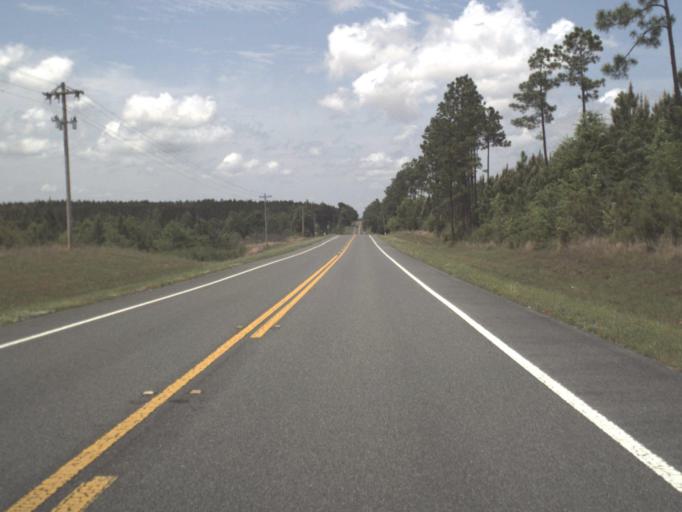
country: US
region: Florida
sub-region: Santa Rosa County
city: Wallace
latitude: 30.8328
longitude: -87.1404
